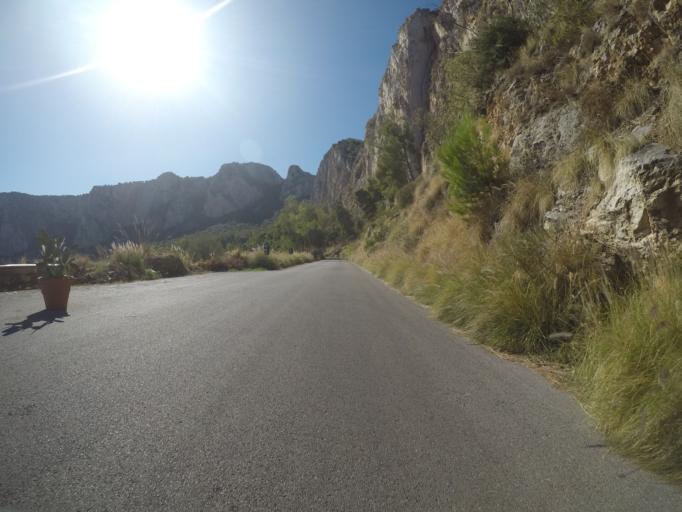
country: IT
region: Sicily
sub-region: Palermo
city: Palermo
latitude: 38.1927
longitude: 13.3392
